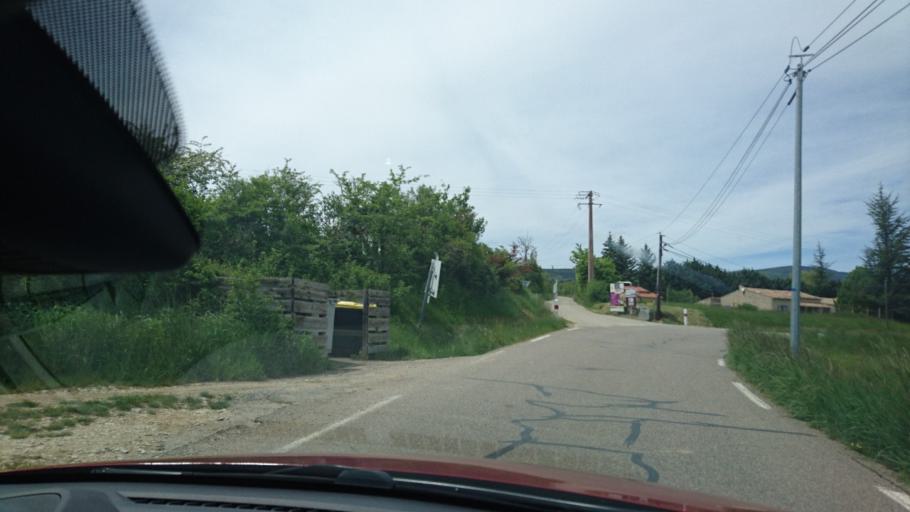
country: FR
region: Provence-Alpes-Cote d'Azur
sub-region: Departement du Vaucluse
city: Sault
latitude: 44.0992
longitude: 5.4030
